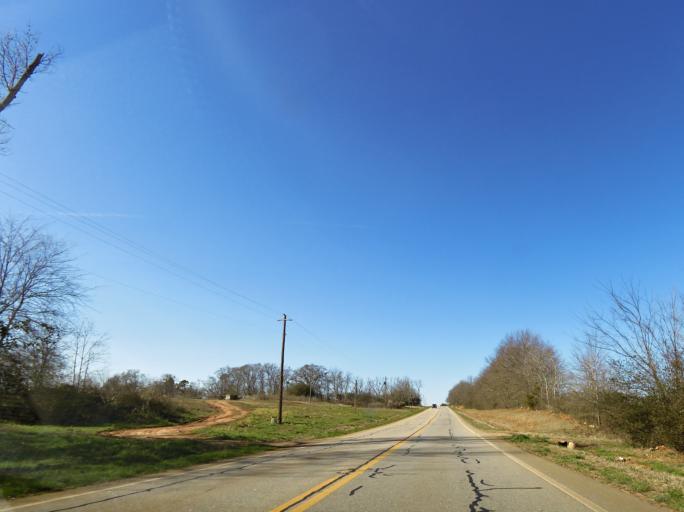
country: US
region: Georgia
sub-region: Lamar County
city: Barnesville
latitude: 32.8835
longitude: -84.0979
